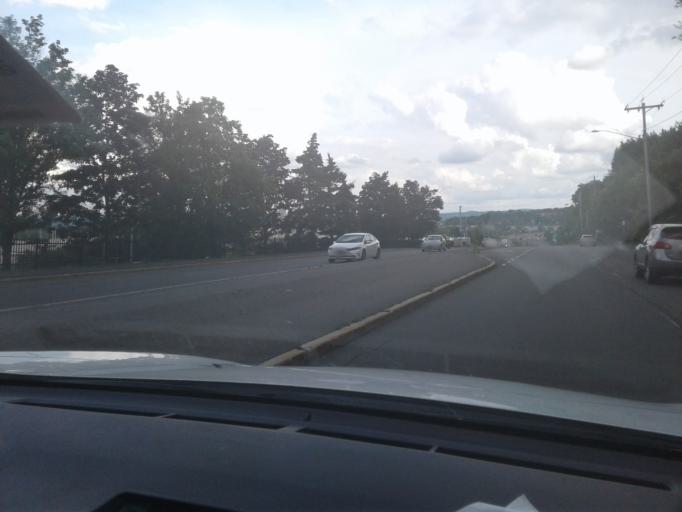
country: US
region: New York
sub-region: Onondaga County
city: East Syracuse
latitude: 43.0651
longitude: -76.0888
